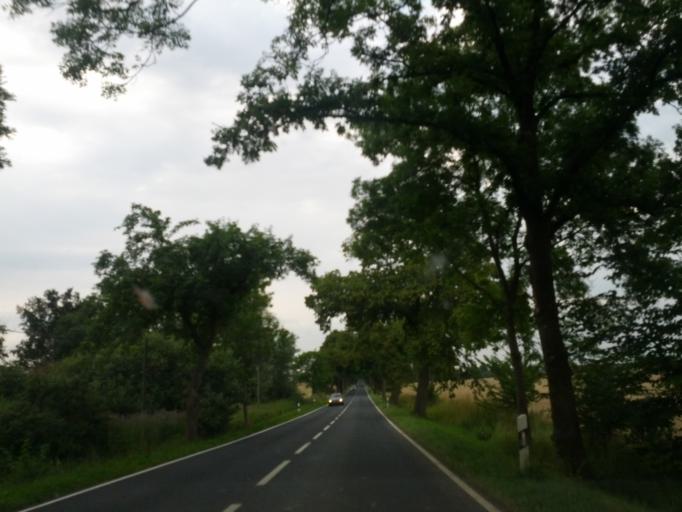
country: DE
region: Mecklenburg-Vorpommern
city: Kropelin
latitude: 54.0121
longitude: 11.8122
